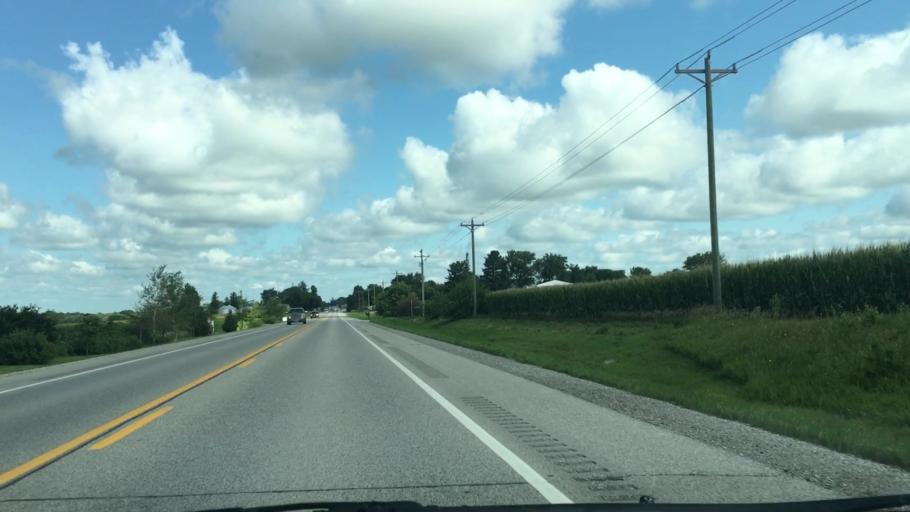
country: US
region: Iowa
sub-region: Johnson County
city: Solon
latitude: 41.7864
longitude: -91.4867
